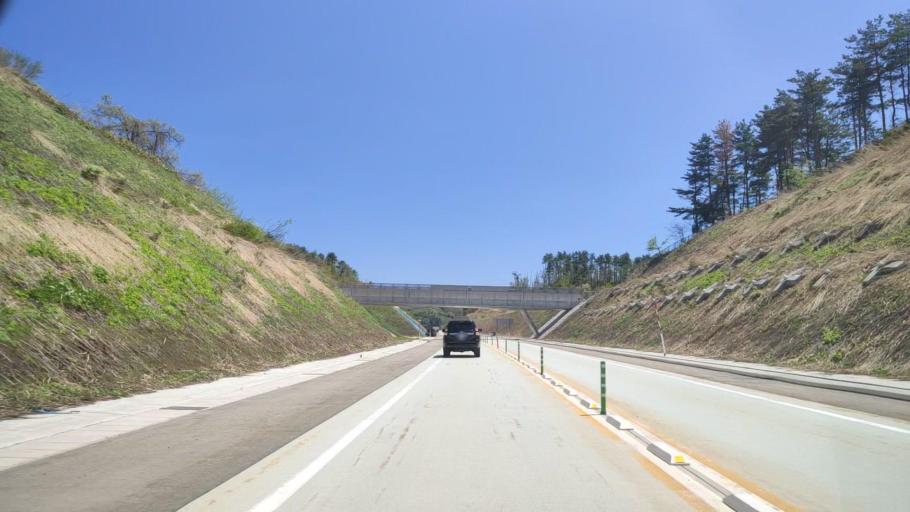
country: JP
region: Yamagata
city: Obanazawa
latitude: 38.5881
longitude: 140.3907
